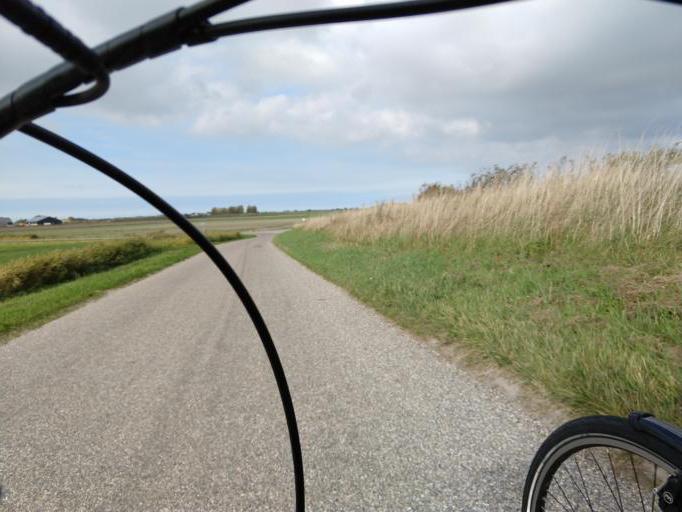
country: NL
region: Zeeland
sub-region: Schouwen-Duiveland
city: Scharendijke
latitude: 51.6928
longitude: 3.9487
